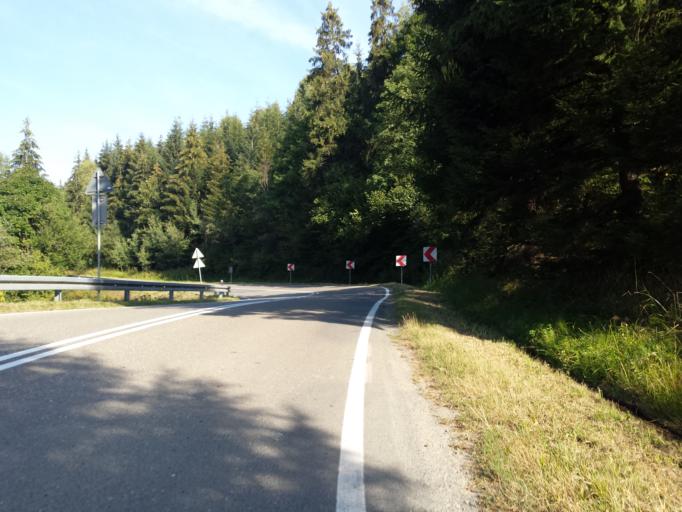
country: PL
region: Subcarpathian Voivodeship
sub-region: Powiat leski
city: Cisna
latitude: 49.2170
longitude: 22.3215
